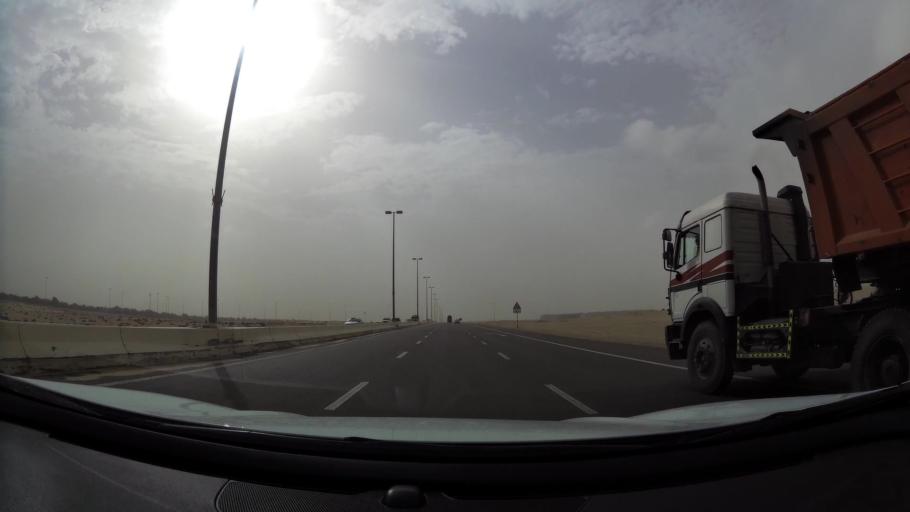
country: AE
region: Abu Dhabi
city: Abu Dhabi
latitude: 24.4693
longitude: 54.6718
